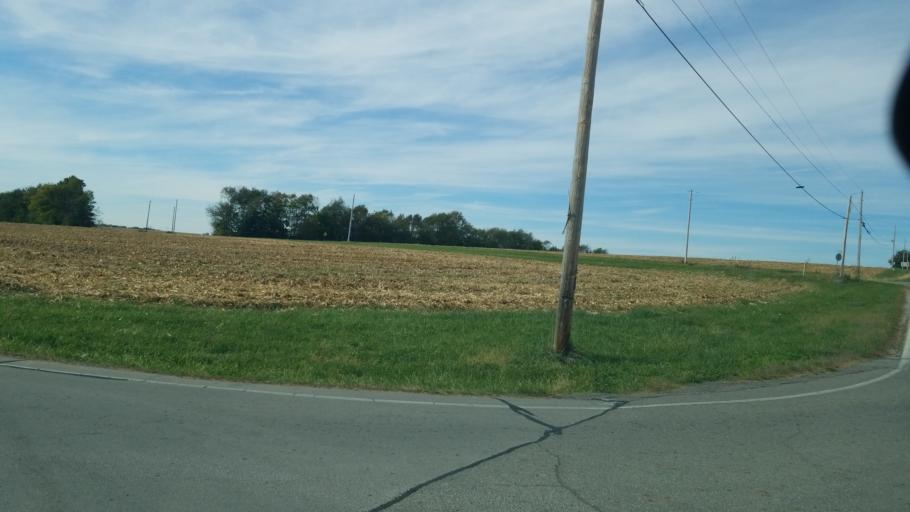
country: US
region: Ohio
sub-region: Highland County
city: Leesburg
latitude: 39.3347
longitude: -83.5496
